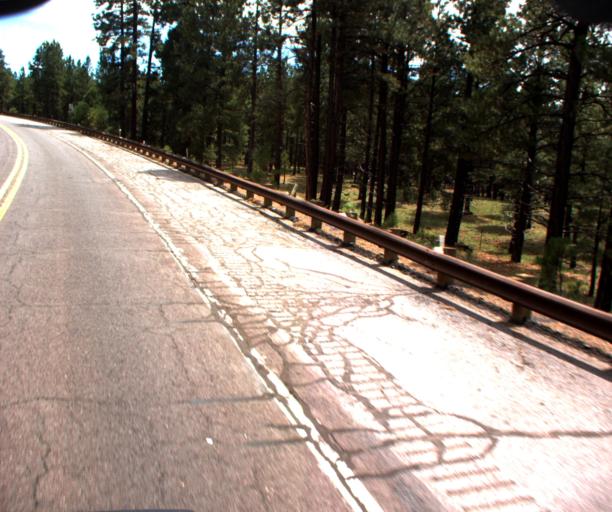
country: US
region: Arizona
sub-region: Coconino County
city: Parks
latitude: 35.4323
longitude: -111.7629
